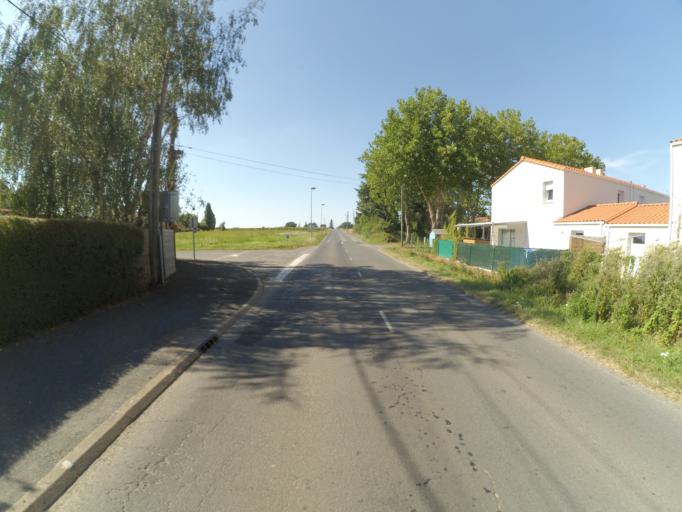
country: FR
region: Pays de la Loire
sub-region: Departement de la Loire-Atlantique
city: Vallet
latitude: 47.1677
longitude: -1.2731
